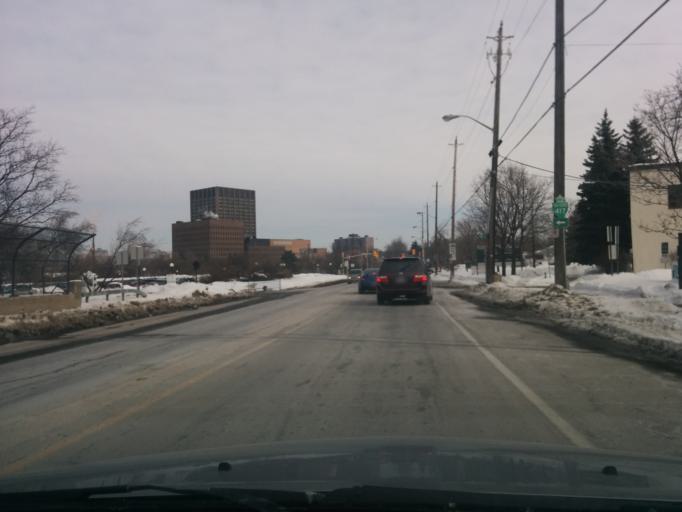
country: CA
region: Ontario
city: Ottawa
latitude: 45.3950
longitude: -75.7079
